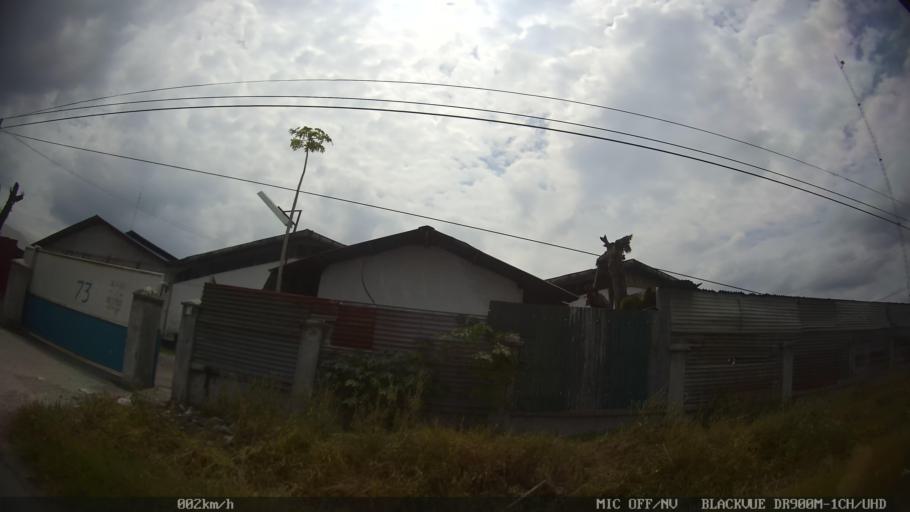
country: ID
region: North Sumatra
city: Sunggal
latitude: 3.6242
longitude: 98.5938
